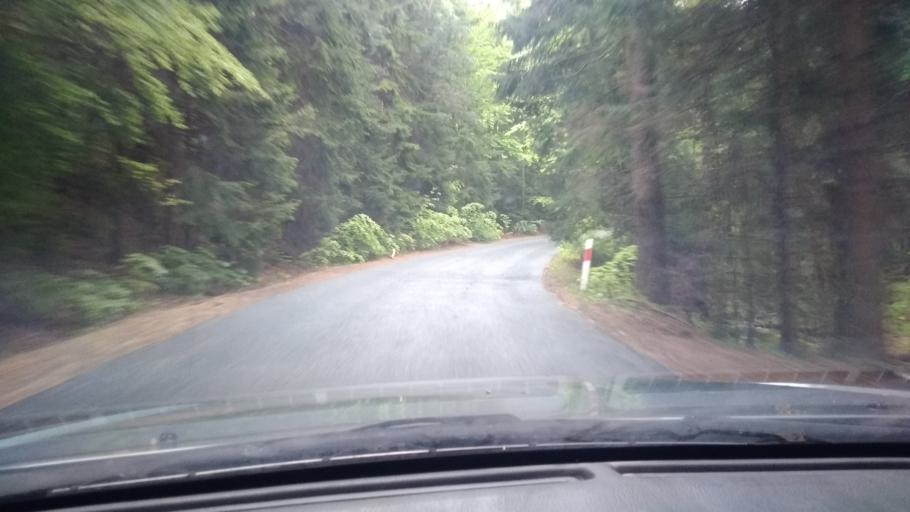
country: PL
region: Lower Silesian Voivodeship
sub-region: Powiat jeleniogorski
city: Podgorzyn
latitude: 50.7966
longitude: 15.6916
